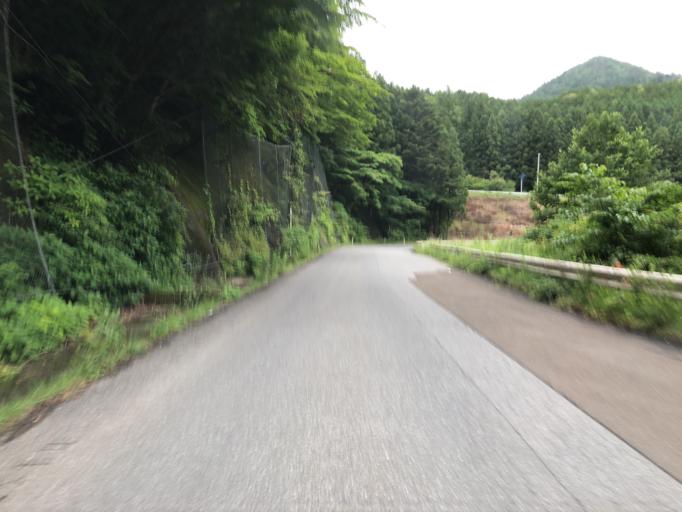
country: JP
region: Fukushima
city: Namie
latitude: 37.6791
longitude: 140.8616
